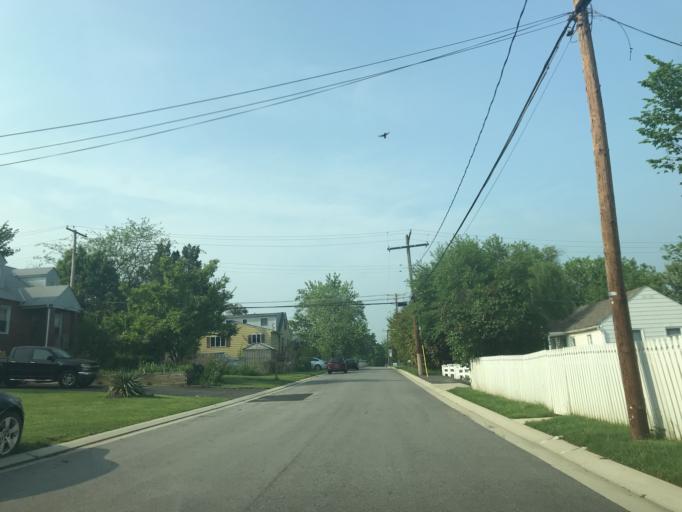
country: US
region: Maryland
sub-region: Baltimore County
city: Parkville
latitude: 39.3826
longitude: -76.5610
